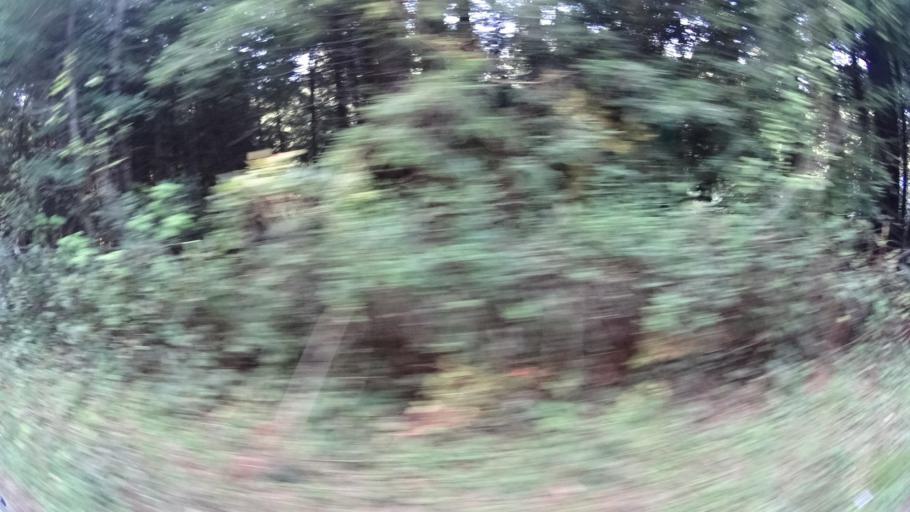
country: US
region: California
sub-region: Humboldt County
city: Bayside
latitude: 40.7529
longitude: -123.9849
